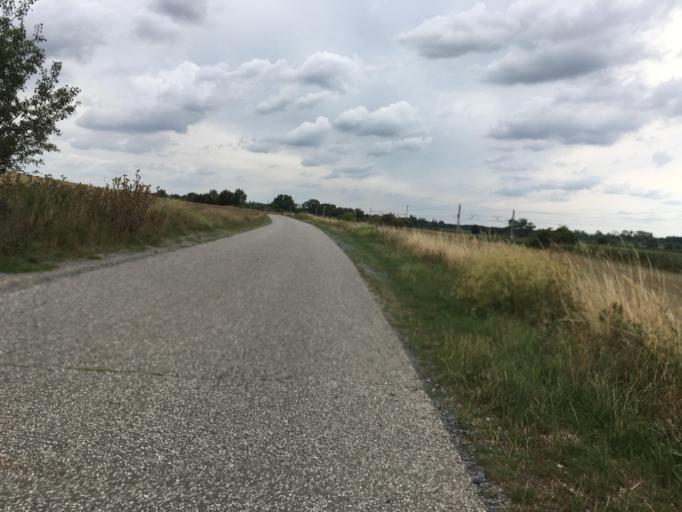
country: DE
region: Brandenburg
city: Prenzlau
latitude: 53.2327
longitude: 13.8749
